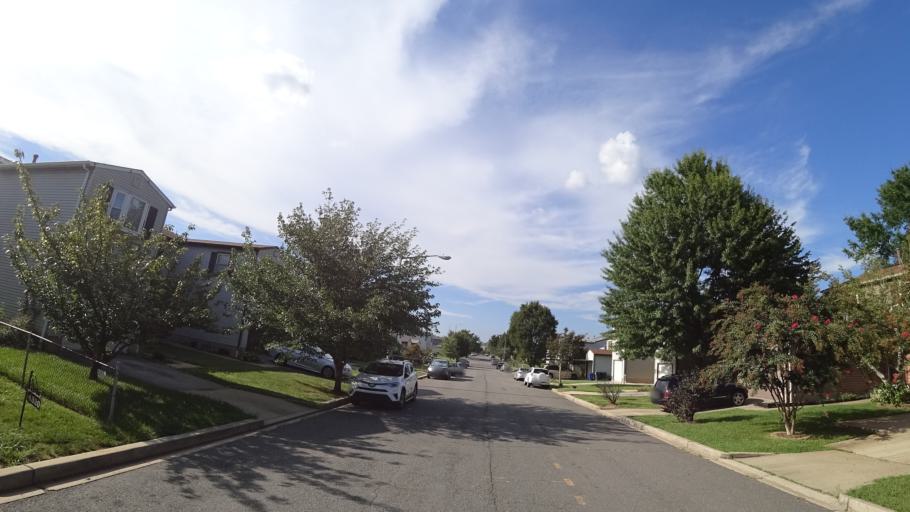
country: US
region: Maryland
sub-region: Prince George's County
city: Chillum
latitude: 38.9417
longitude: -76.9968
